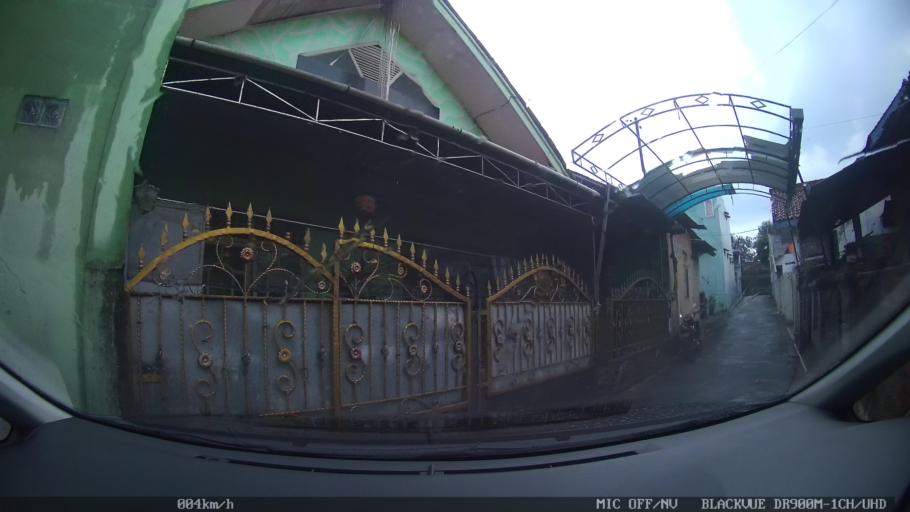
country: ID
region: Lampung
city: Kedaton
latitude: -5.3936
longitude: 105.2908
